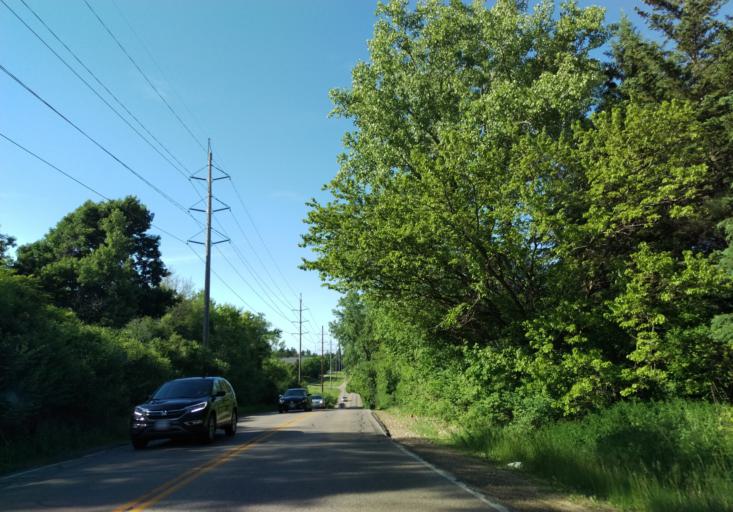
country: US
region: Wisconsin
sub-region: Dane County
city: Middleton
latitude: 43.0774
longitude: -89.5369
